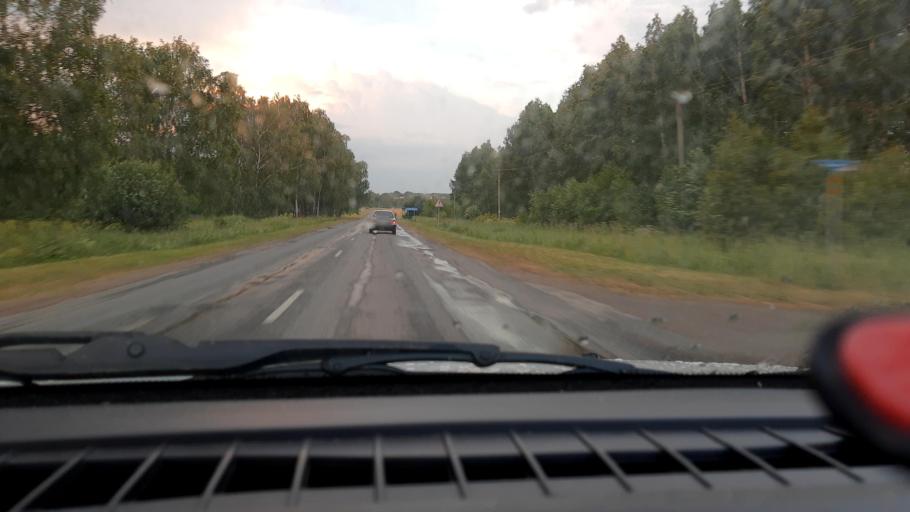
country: RU
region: Nizjnij Novgorod
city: Afonino
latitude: 56.1211
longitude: 43.9980
